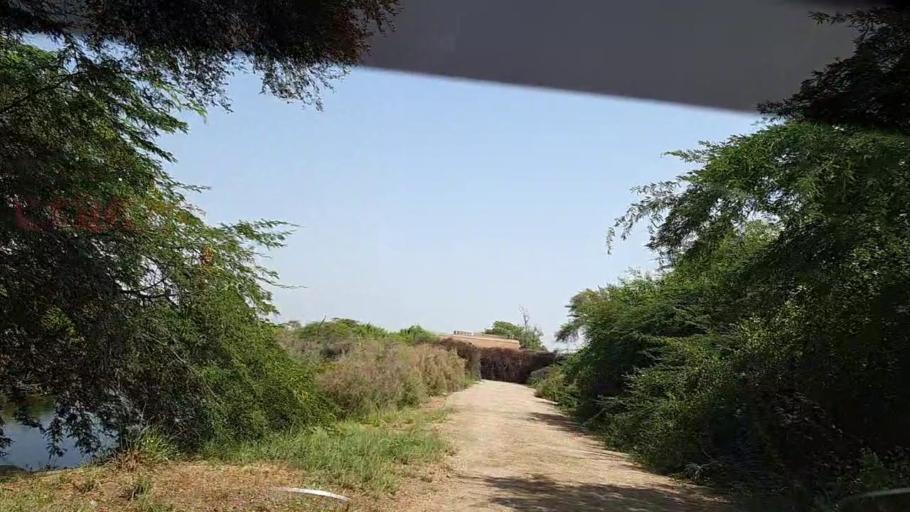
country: PK
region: Sindh
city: Rajo Khanani
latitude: 24.9263
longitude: 68.8780
